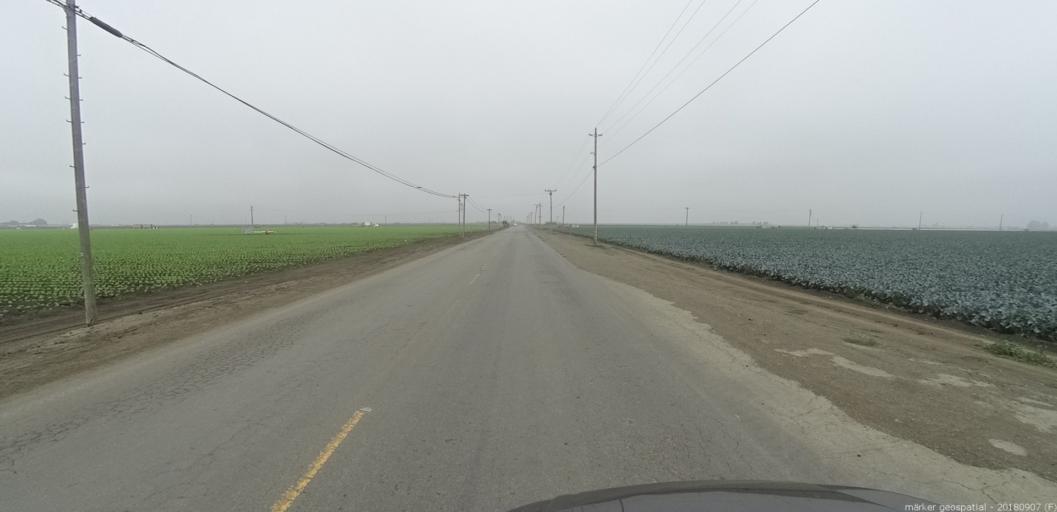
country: US
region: California
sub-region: Monterey County
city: Castroville
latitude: 36.7344
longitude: -121.7582
